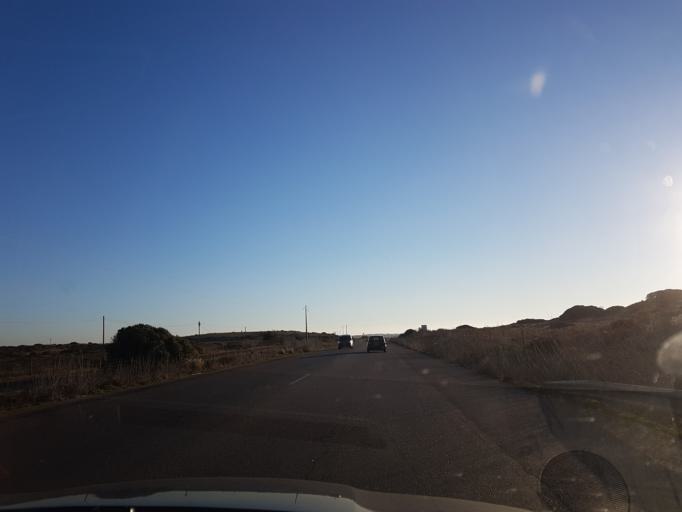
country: PT
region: Faro
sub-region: Vila do Bispo
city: Sagres
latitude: 37.0354
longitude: -8.9342
